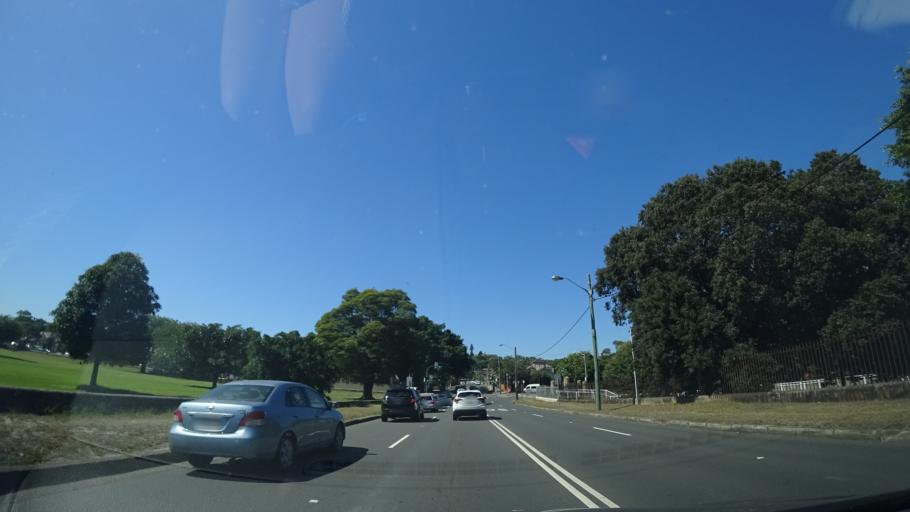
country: AU
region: New South Wales
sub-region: Waverley
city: Bondi Junction
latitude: -33.9020
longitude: 151.2450
